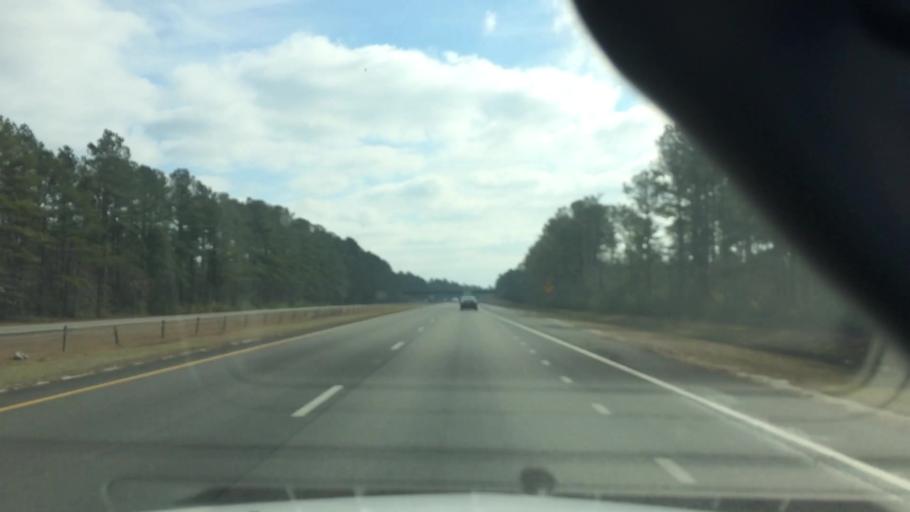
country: US
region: North Carolina
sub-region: Pender County
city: Burgaw
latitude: 34.5703
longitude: -77.8997
